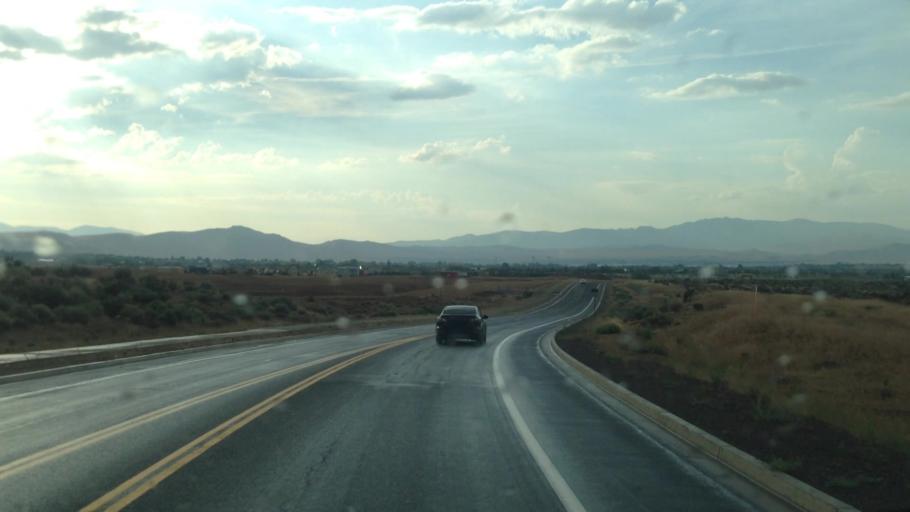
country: US
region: Nevada
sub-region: Washoe County
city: Lemmon Valley
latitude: 39.6150
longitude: -119.8571
